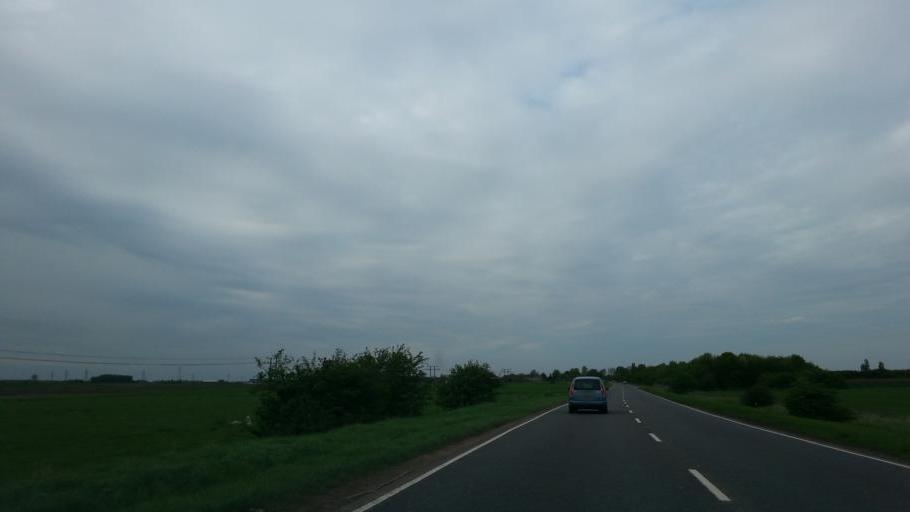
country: GB
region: England
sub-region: Cambridgeshire
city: March
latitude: 52.5372
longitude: 0.0695
